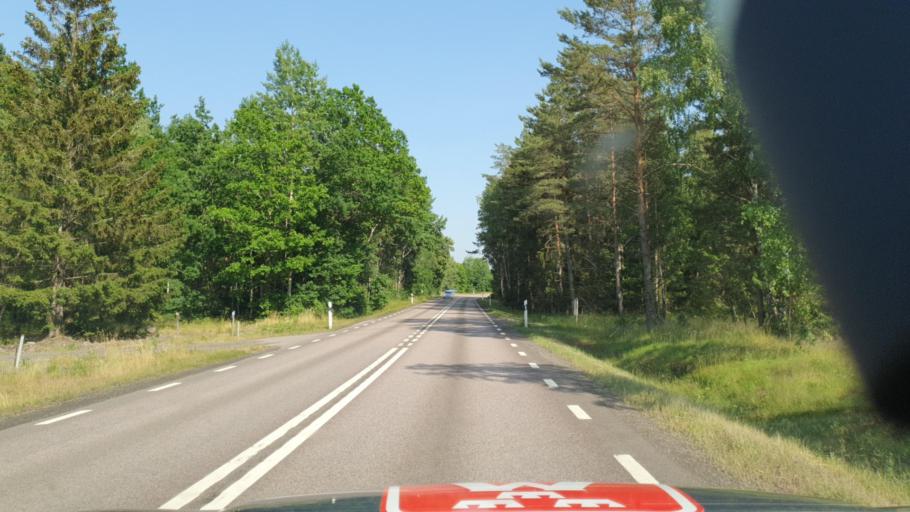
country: SE
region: Kalmar
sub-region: Nybro Kommun
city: Nybro
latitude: 56.7723
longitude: 15.8522
